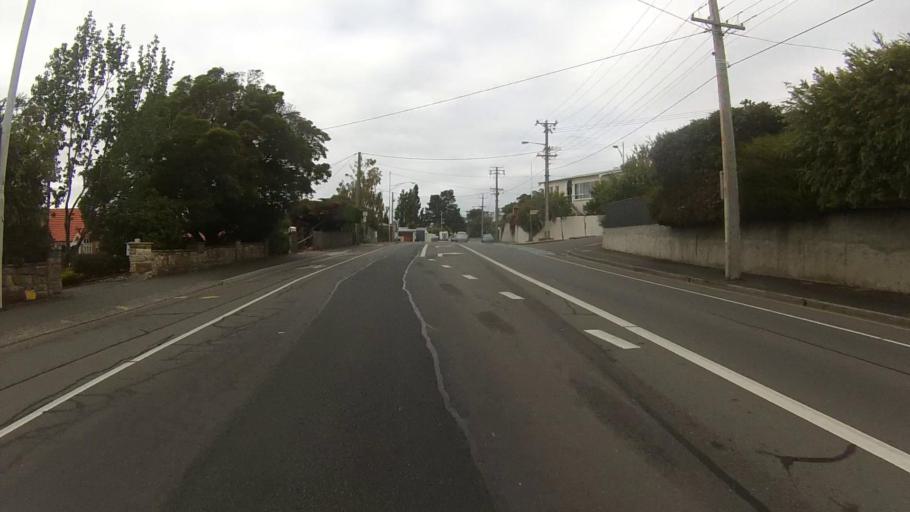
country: AU
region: Tasmania
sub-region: Kingborough
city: Taroona
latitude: -42.9165
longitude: 147.3589
